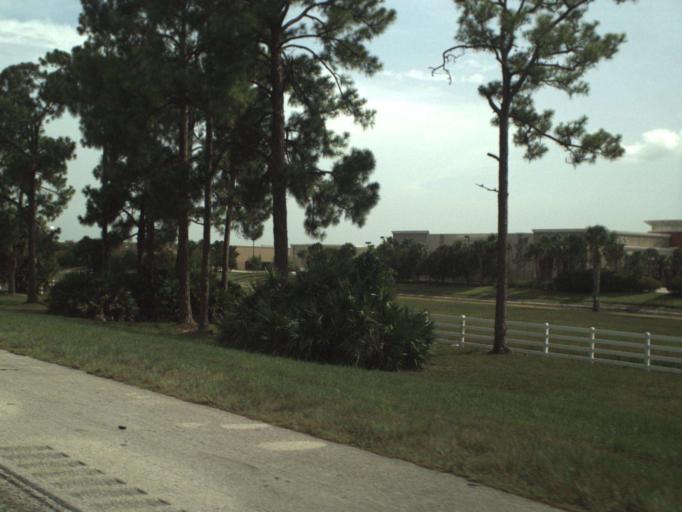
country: US
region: Florida
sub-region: Saint Lucie County
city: Port Saint Lucie
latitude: 27.2730
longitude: -80.4256
